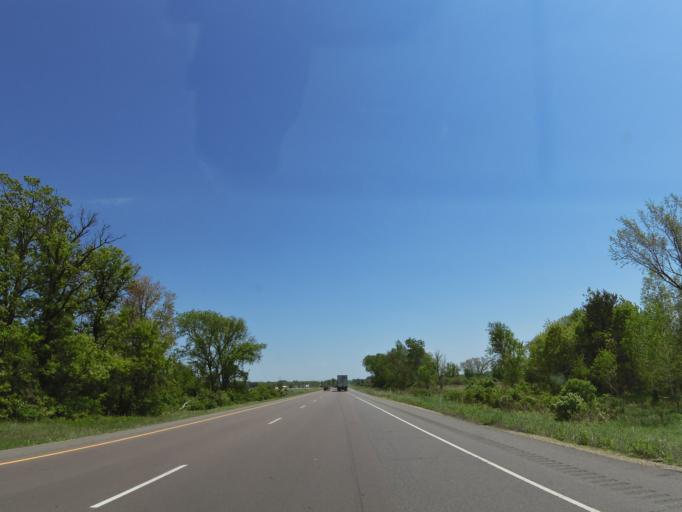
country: US
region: Wisconsin
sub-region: Monroe County
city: Tomah
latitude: 43.9608
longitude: -90.3724
